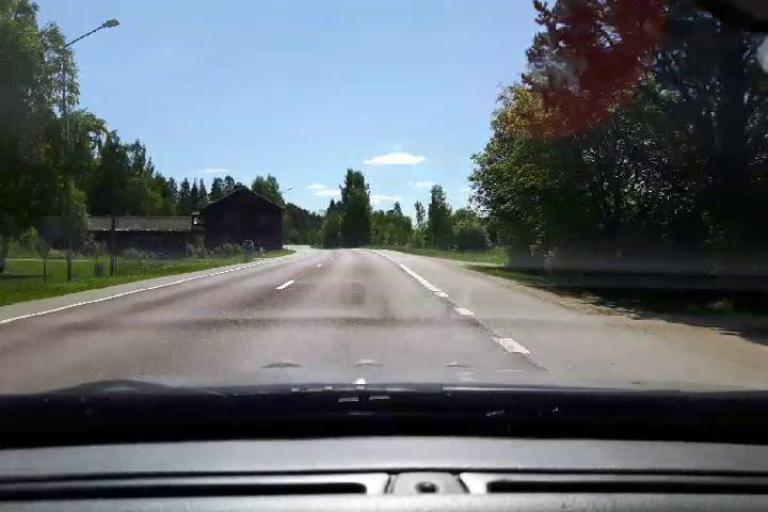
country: SE
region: Jaemtland
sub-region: Harjedalens Kommun
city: Sveg
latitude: 62.1674
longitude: 14.9505
